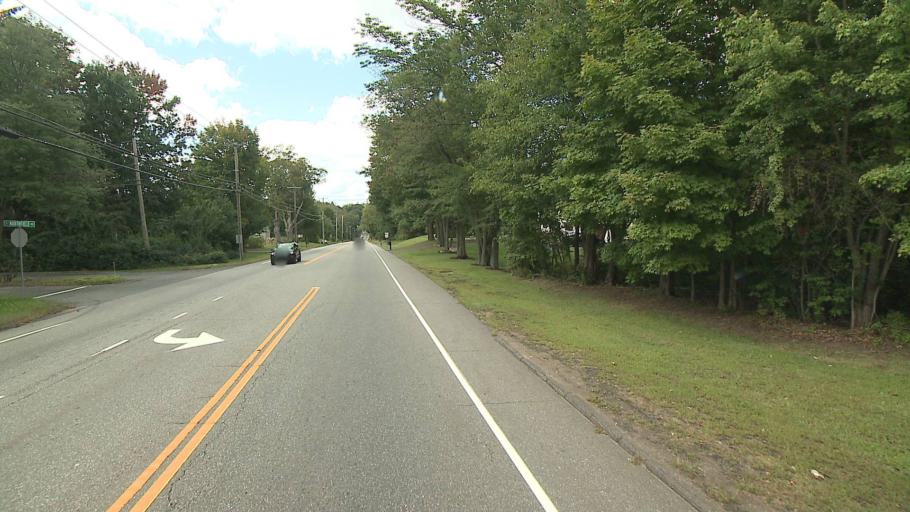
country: US
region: Connecticut
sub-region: Tolland County
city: Coventry Lake
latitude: 41.7977
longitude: -72.3938
